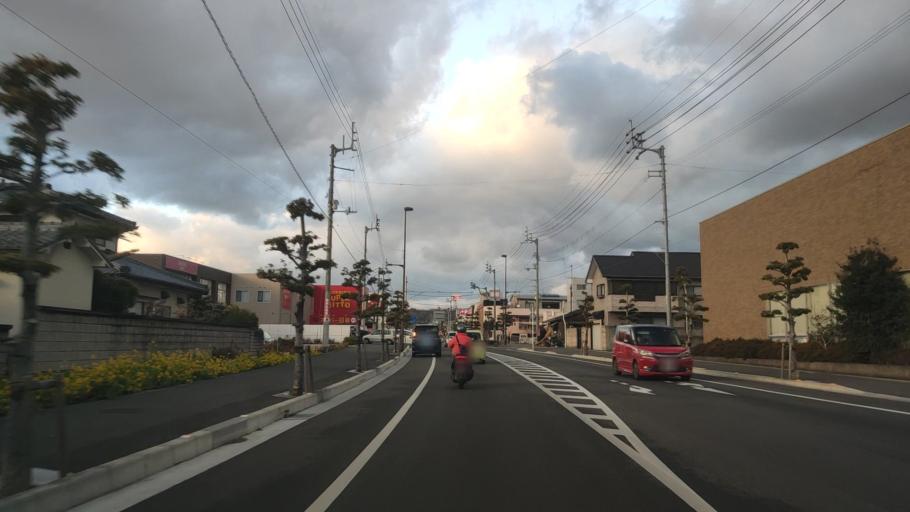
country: JP
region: Ehime
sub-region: Shikoku-chuo Shi
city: Matsuyama
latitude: 33.8302
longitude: 132.7875
